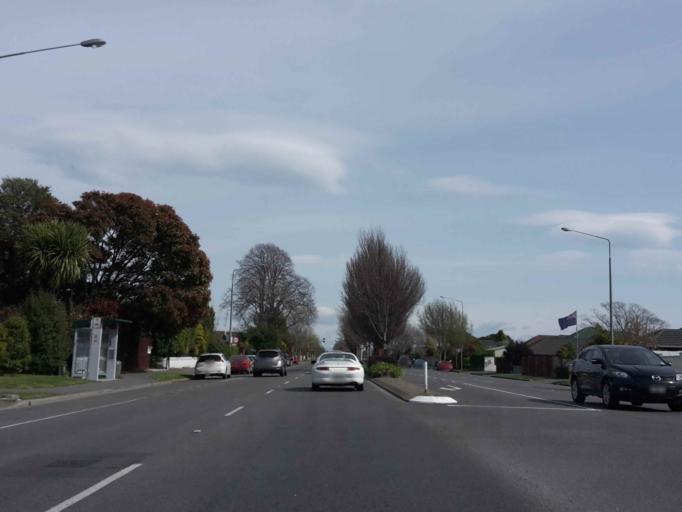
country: NZ
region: Canterbury
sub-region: Selwyn District
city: Prebbleton
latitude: -43.5288
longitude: 172.5618
